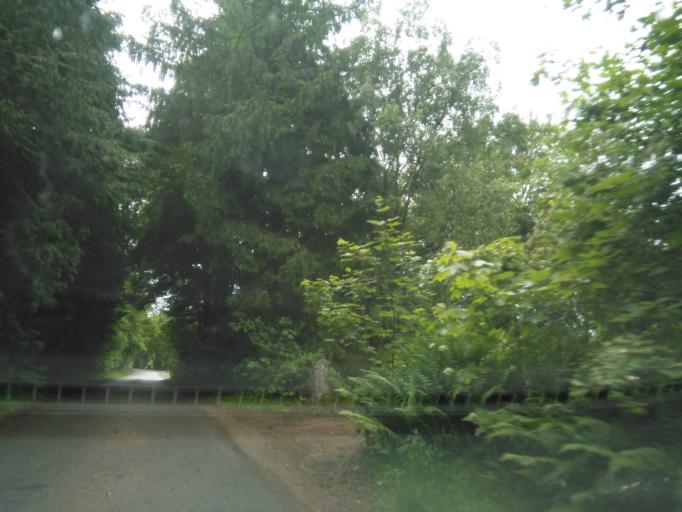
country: DK
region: Capital Region
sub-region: Bornholm Kommune
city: Nexo
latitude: 55.0940
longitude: 15.1108
